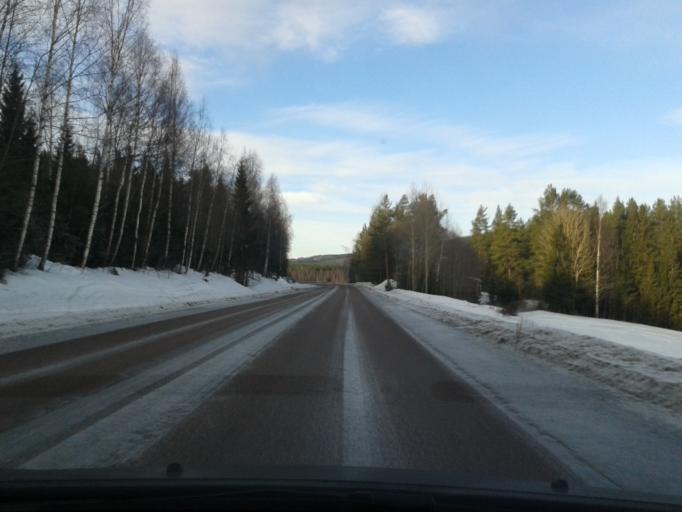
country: SE
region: Vaesternorrland
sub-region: OErnskoeldsviks Kommun
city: Bjasta
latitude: 63.3445
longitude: 18.5022
